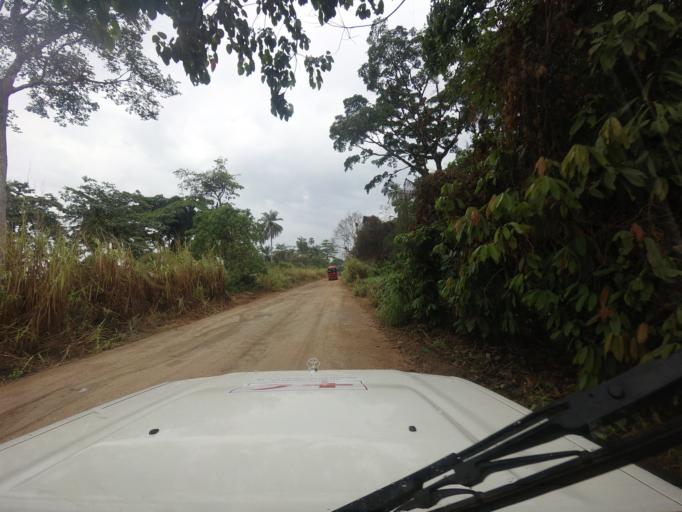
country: SL
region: Eastern Province
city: Buedu
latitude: 8.3457
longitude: -10.1797
